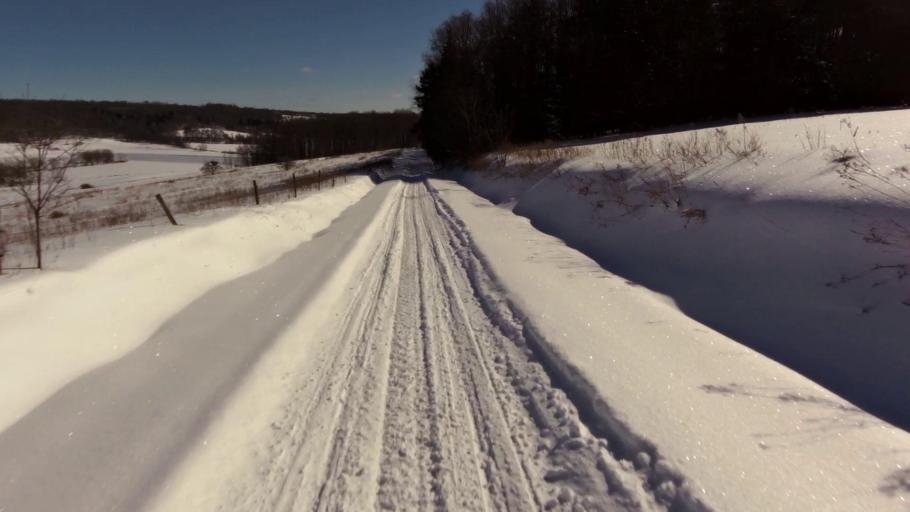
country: US
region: New York
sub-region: Chautauqua County
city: Silver Creek
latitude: 42.3832
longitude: -79.1243
